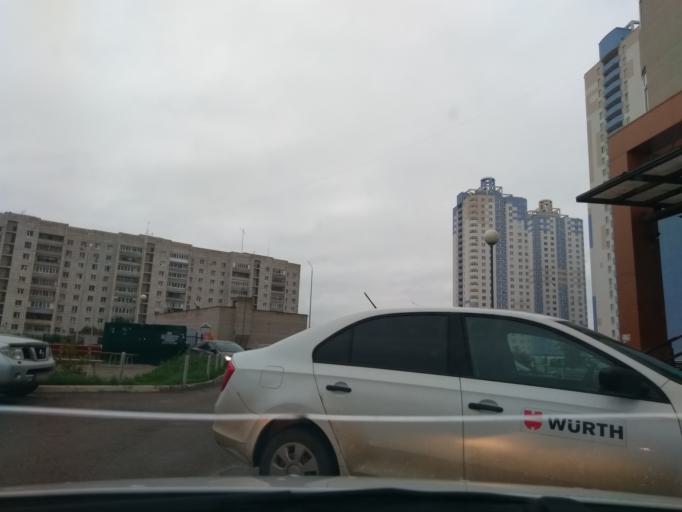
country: RU
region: Perm
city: Perm
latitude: 58.0067
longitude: 56.3220
